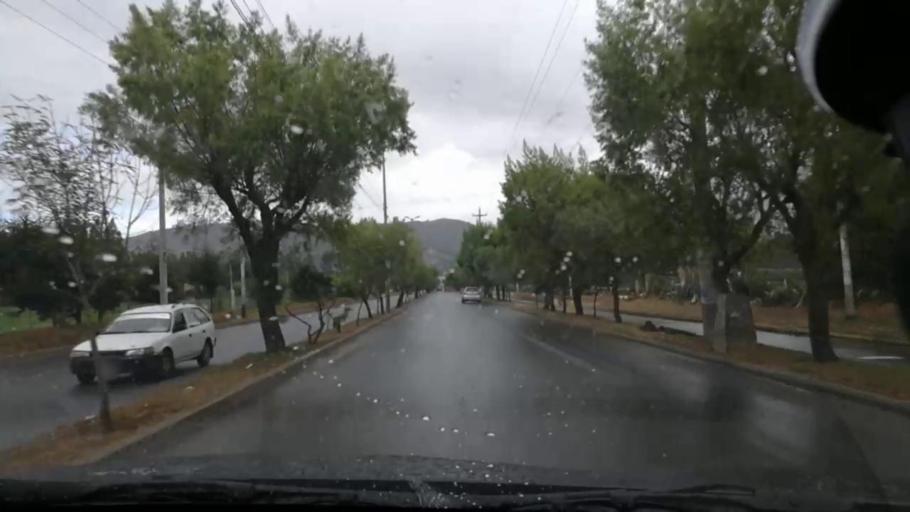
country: PE
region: Cajamarca
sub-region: Provincia de Cajamarca
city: Cajamarca
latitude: -7.1652
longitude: -78.4846
